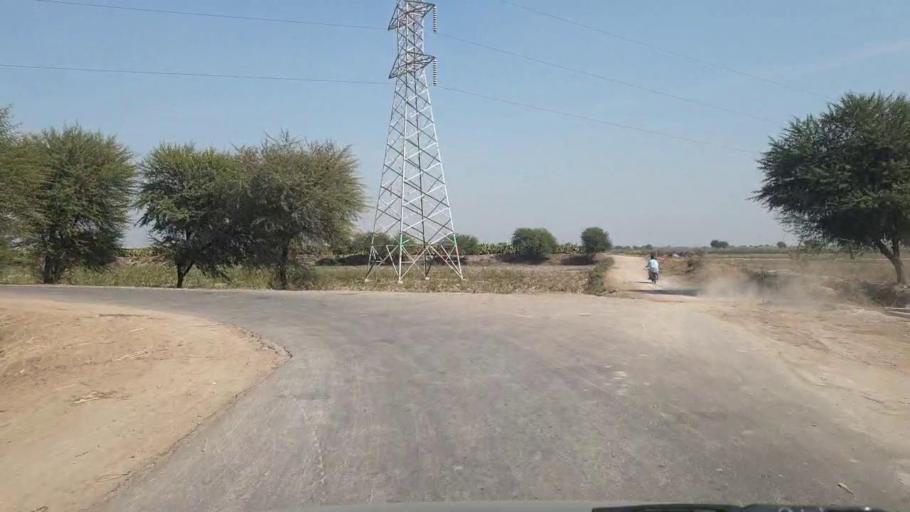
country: PK
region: Sindh
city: Chambar
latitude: 25.3117
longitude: 68.8165
